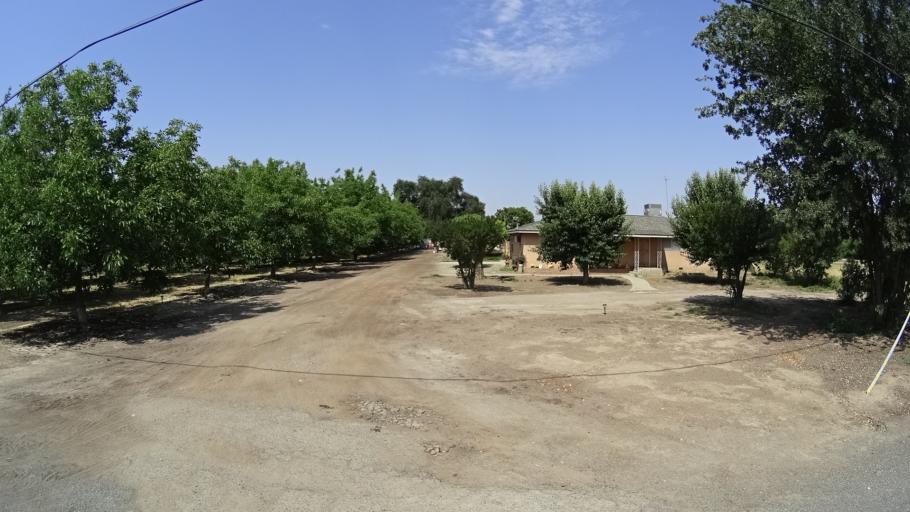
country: US
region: California
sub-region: Fresno County
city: Laton
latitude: 36.3980
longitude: -119.7624
